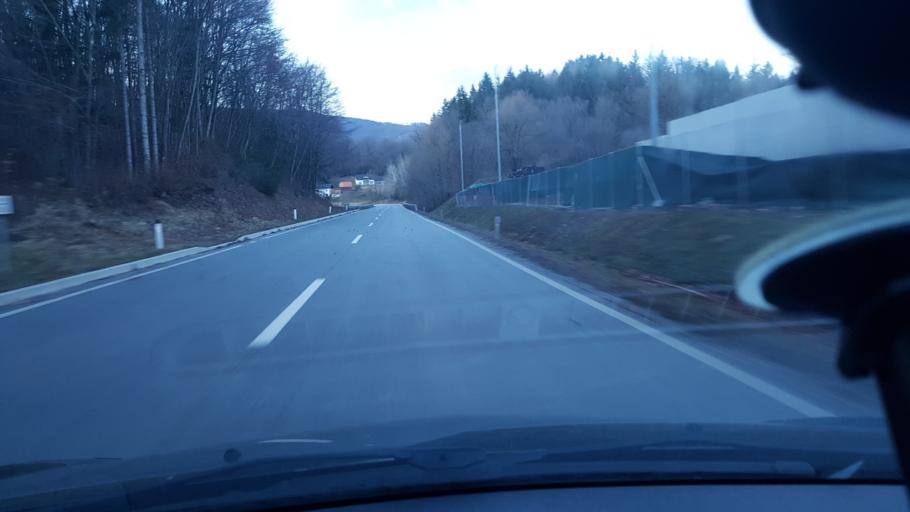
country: SI
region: Rogatec
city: Rogatec
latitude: 46.2367
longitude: 15.6713
